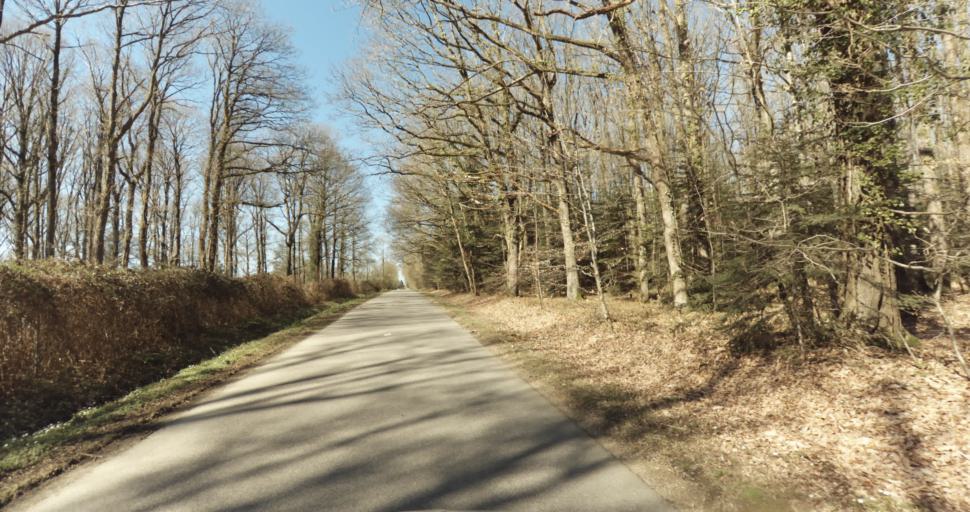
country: FR
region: Lower Normandy
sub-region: Departement du Calvados
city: Livarot
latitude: 48.9665
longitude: 0.0827
